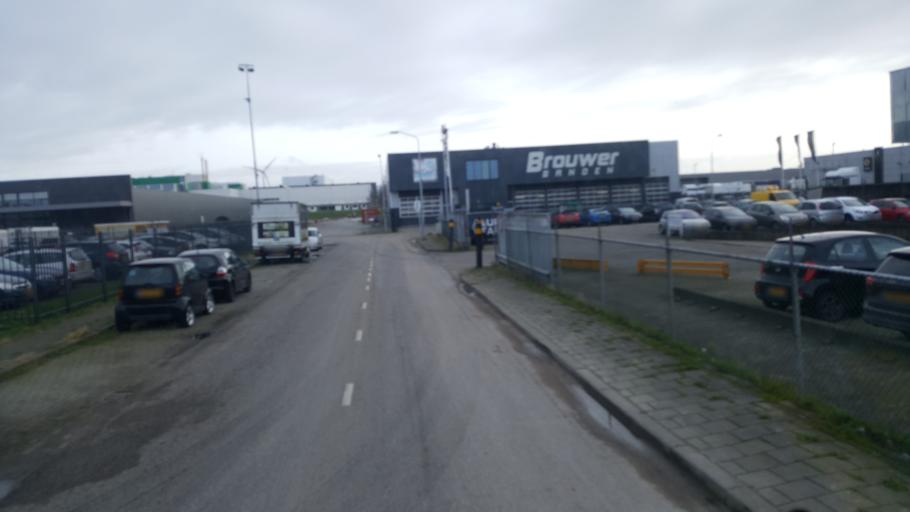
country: NL
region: North Holland
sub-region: Gemeente Zaanstad
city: Zaanstad
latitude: 52.4269
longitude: 4.7949
